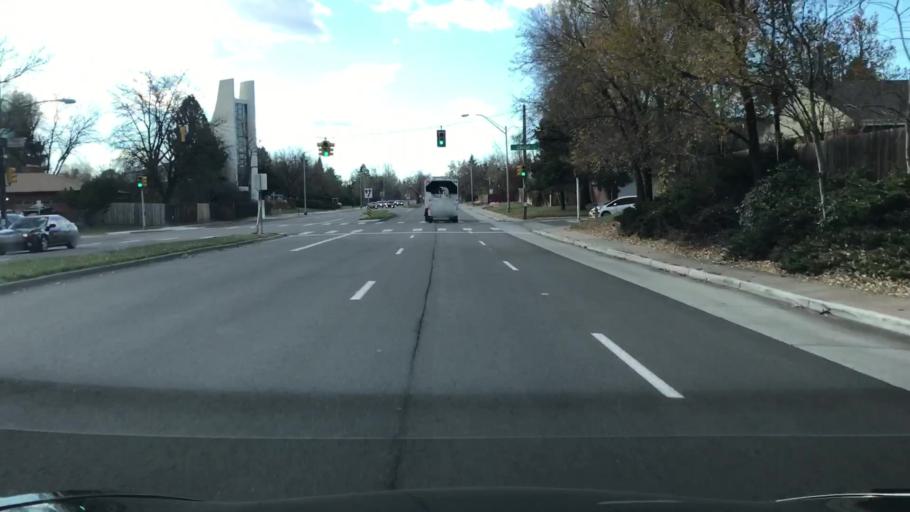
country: US
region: Colorado
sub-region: Arapahoe County
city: Glendale
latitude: 39.6632
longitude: -104.9130
